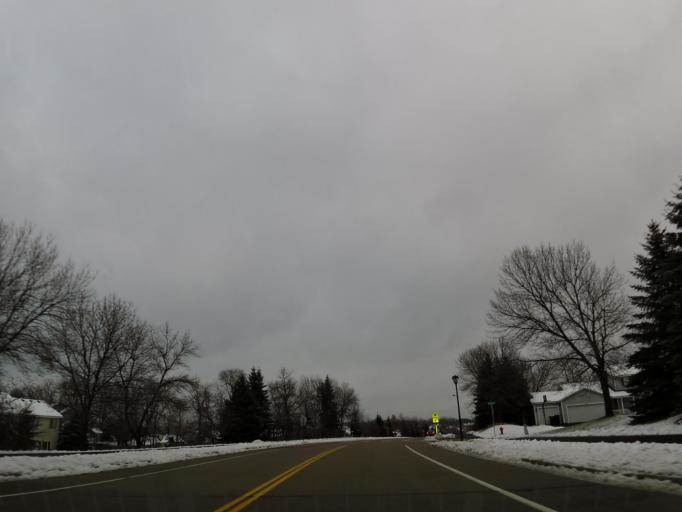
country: US
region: Minnesota
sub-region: Dakota County
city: Apple Valley
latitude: 44.7100
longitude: -93.2445
